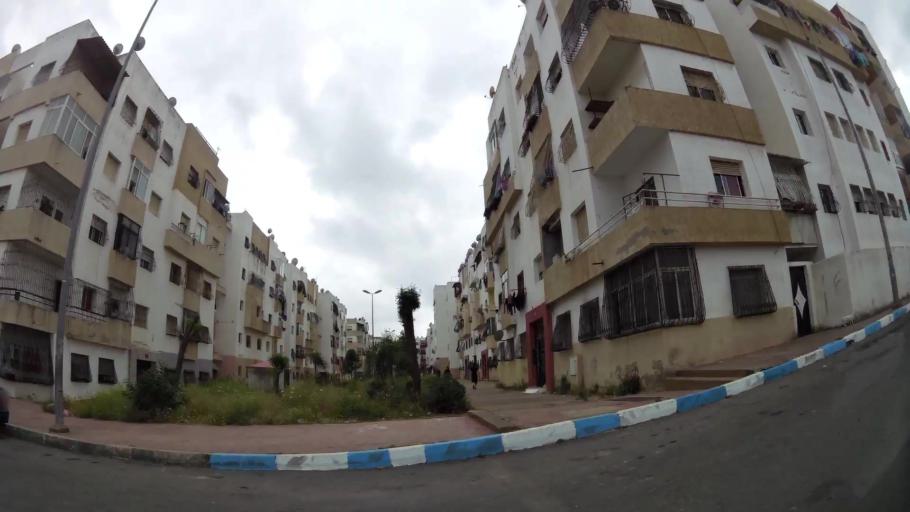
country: MA
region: Rabat-Sale-Zemmour-Zaer
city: Sale
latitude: 34.0409
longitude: -6.7993
